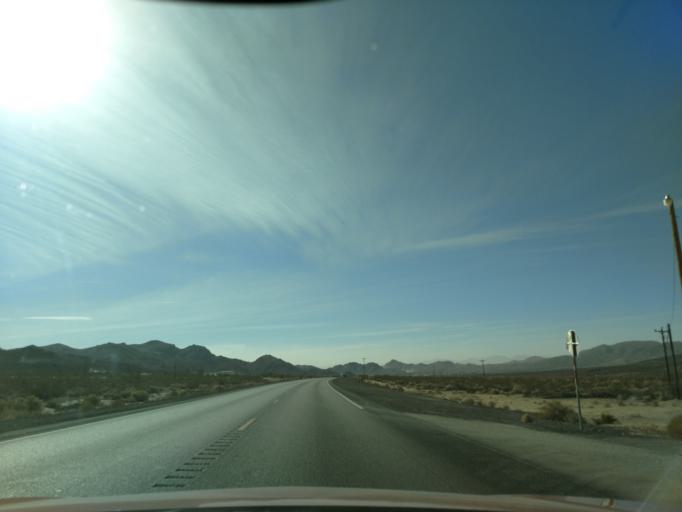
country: US
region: Nevada
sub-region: Nye County
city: Beatty
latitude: 36.9397
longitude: -116.7232
